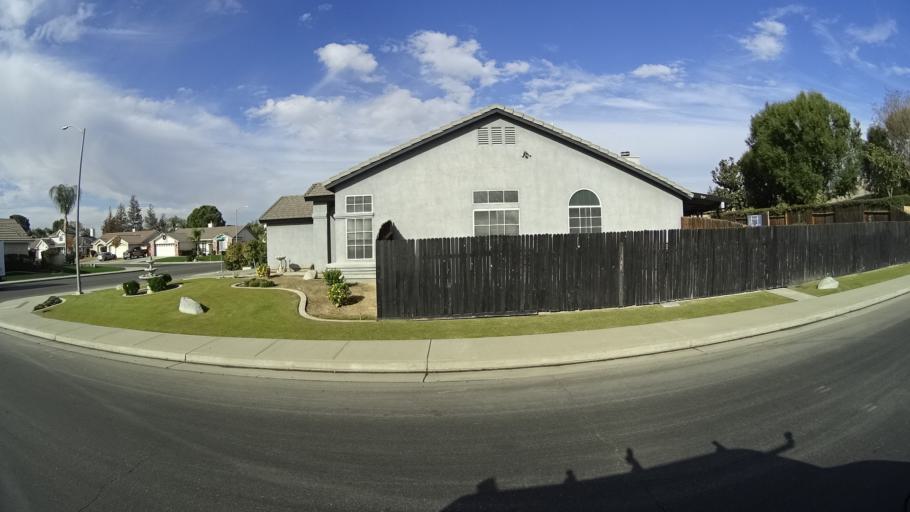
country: US
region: California
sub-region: Kern County
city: Greenacres
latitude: 35.4014
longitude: -119.1233
